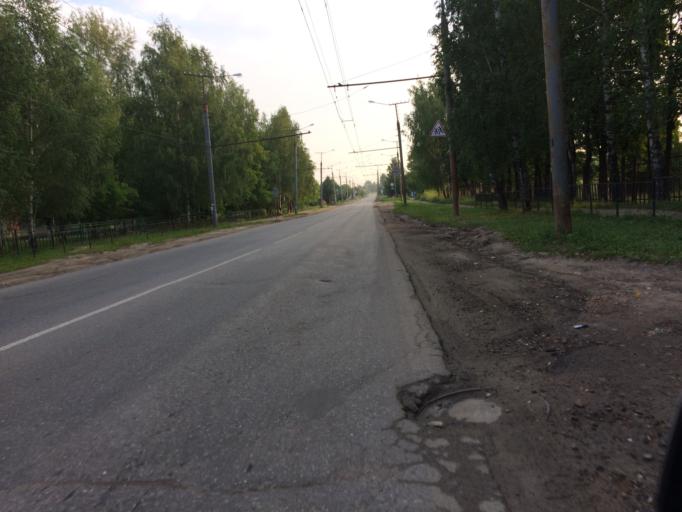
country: RU
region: Mariy-El
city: Yoshkar-Ola
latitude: 56.6410
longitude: 47.9540
